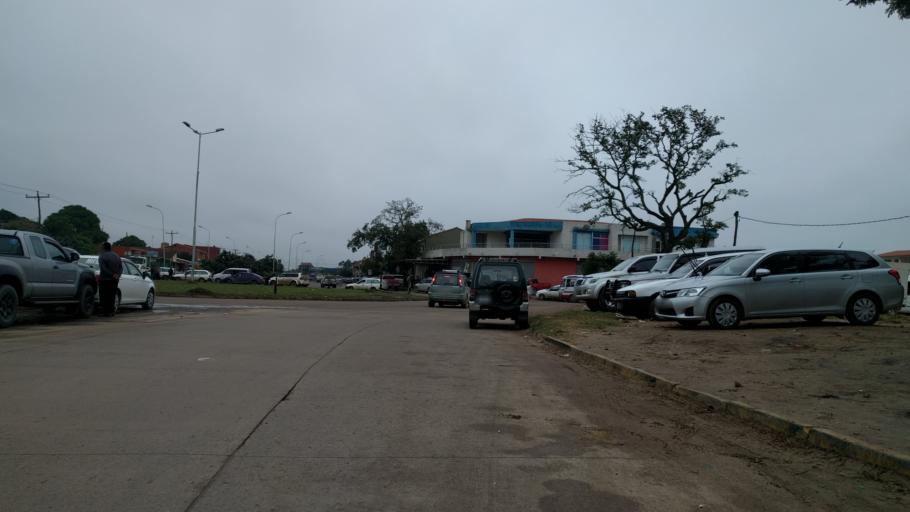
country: BO
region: Santa Cruz
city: Santa Cruz de la Sierra
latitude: -17.8297
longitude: -63.1997
